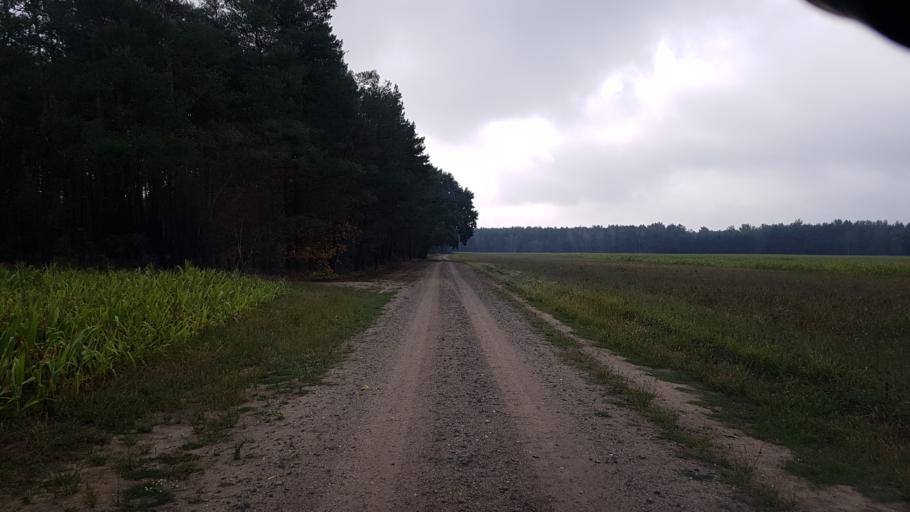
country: DE
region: Brandenburg
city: Ruckersdorf
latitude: 51.5593
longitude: 13.5626
